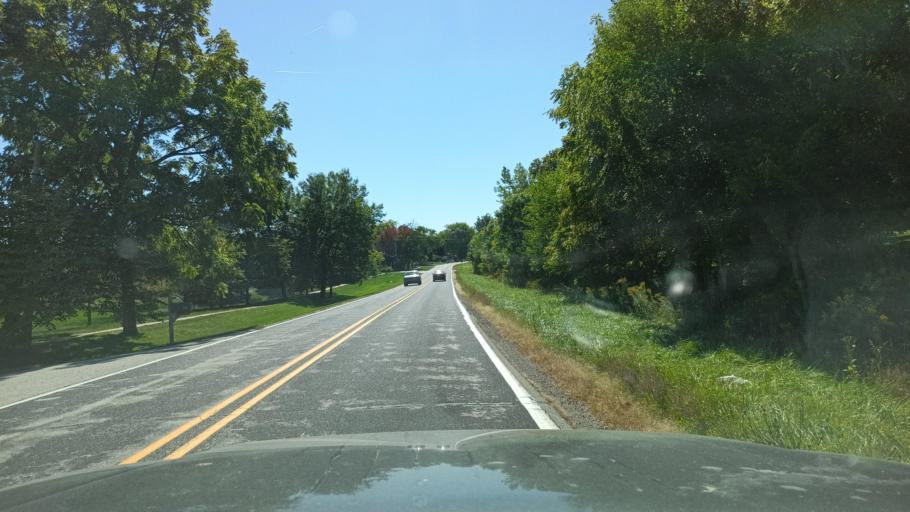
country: US
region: Illinois
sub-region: Champaign County
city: Lake of the Woods
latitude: 40.2061
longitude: -88.3703
